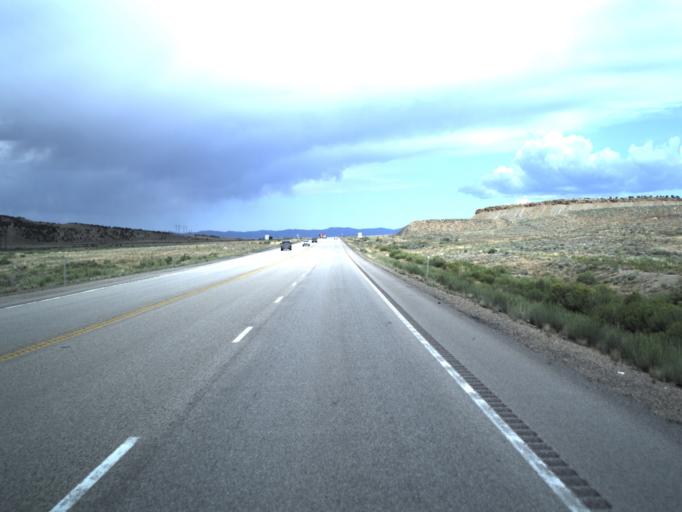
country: US
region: Utah
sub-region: Carbon County
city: Wellington
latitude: 39.5411
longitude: -110.6088
